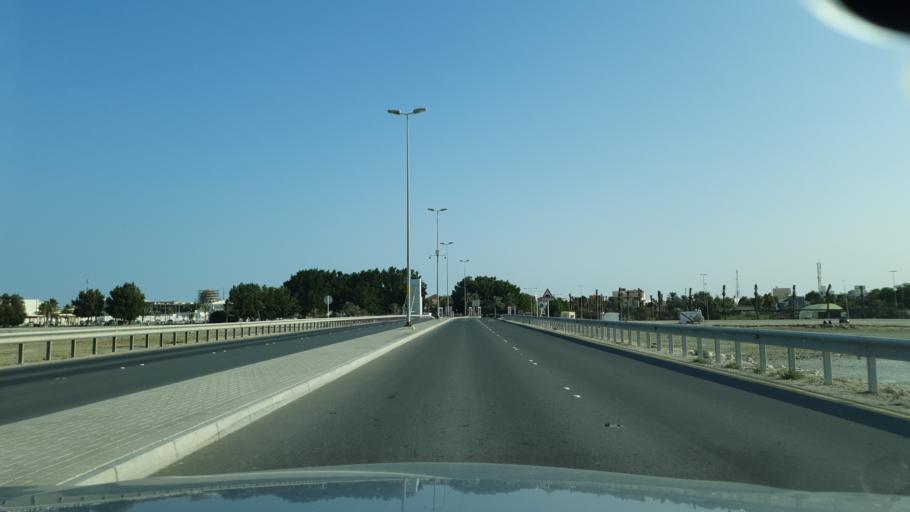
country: BH
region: Manama
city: Jidd Hafs
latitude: 26.2257
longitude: 50.4581
